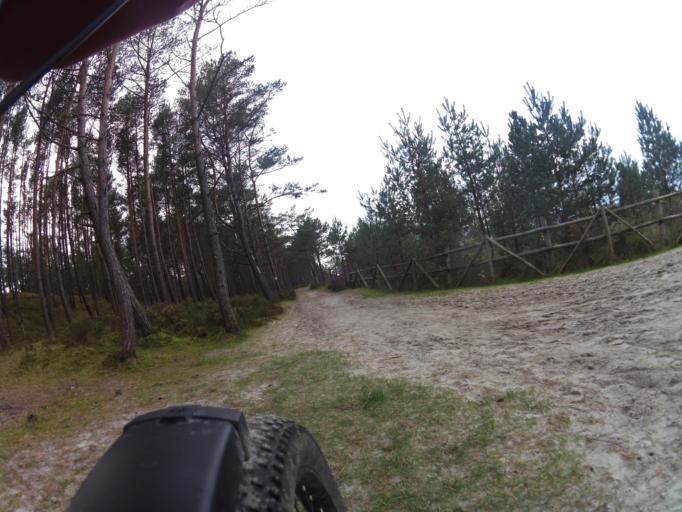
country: PL
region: Pomeranian Voivodeship
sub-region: Powiat wejherowski
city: Choczewo
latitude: 54.8072
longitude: 17.8081
